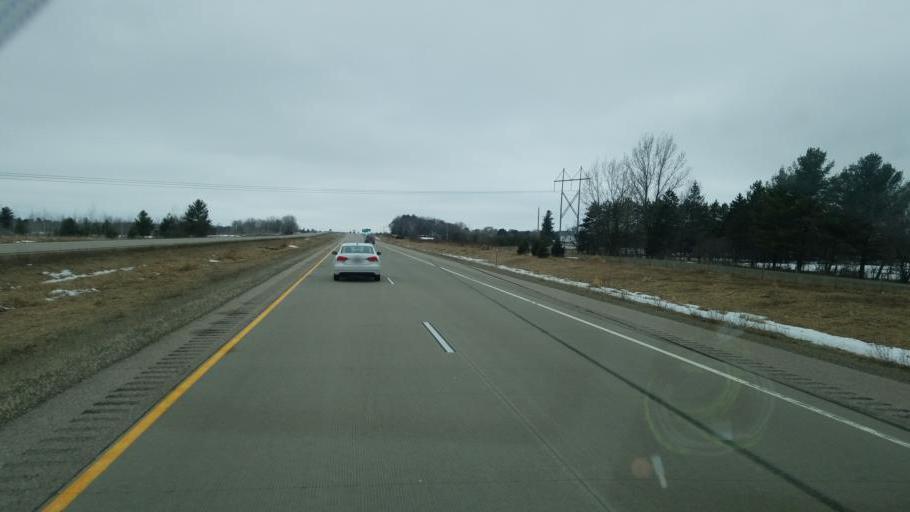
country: US
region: Wisconsin
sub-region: Portage County
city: Stevens Point
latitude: 44.5980
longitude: -89.7017
